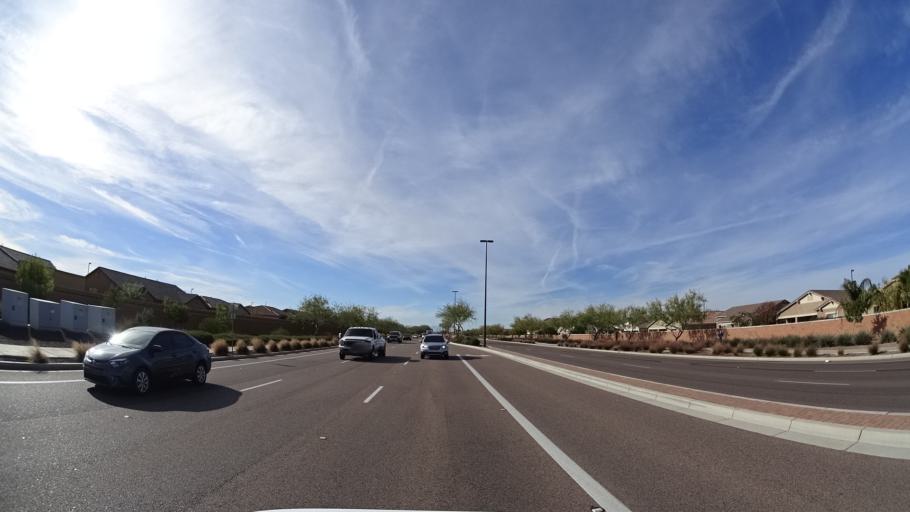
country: US
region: Arizona
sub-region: Maricopa County
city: Queen Creek
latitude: 33.2776
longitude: -111.7255
